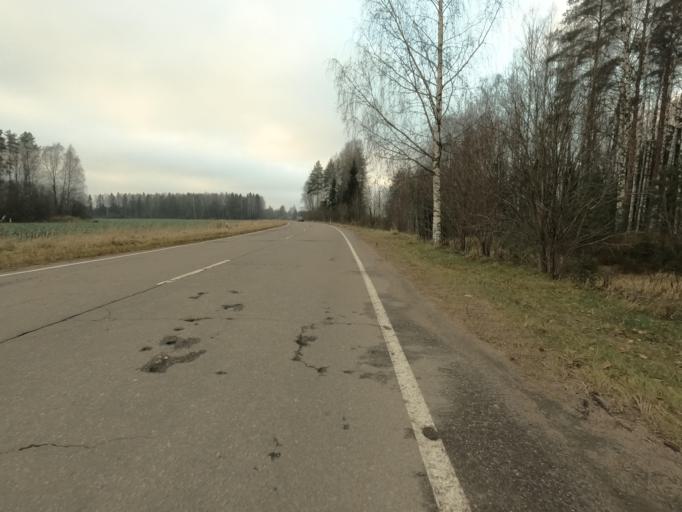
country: RU
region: Leningrad
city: Kirovsk
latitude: 59.8004
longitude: 30.9983
